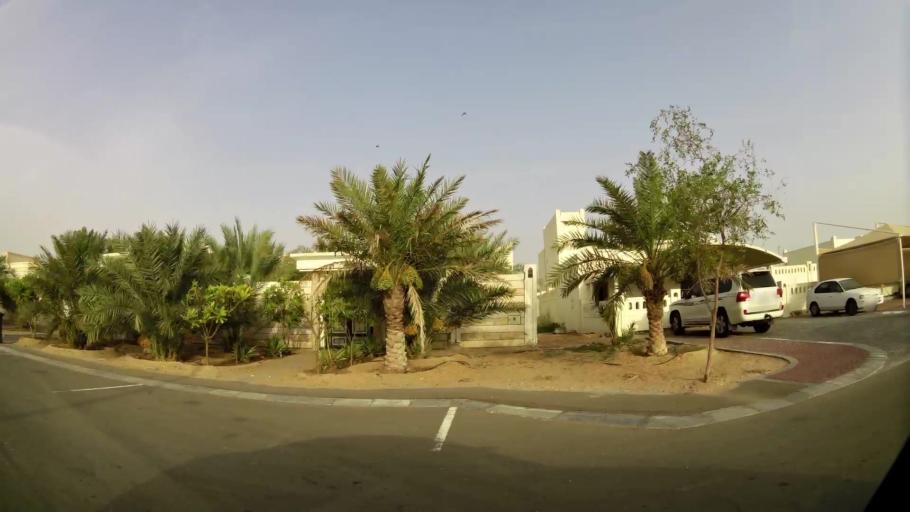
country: AE
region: Abu Dhabi
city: Al Ain
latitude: 24.1136
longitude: 55.7142
